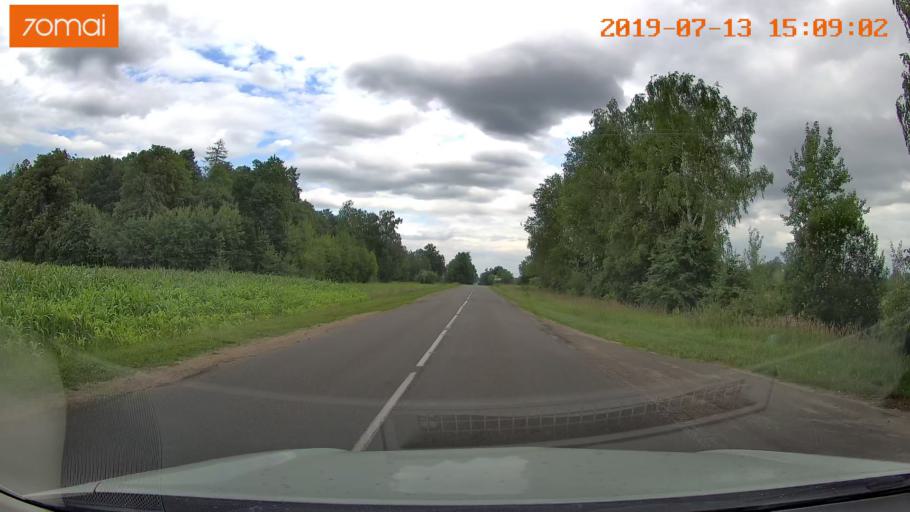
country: BY
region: Mogilev
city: Hlusha
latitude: 53.1744
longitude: 28.7556
